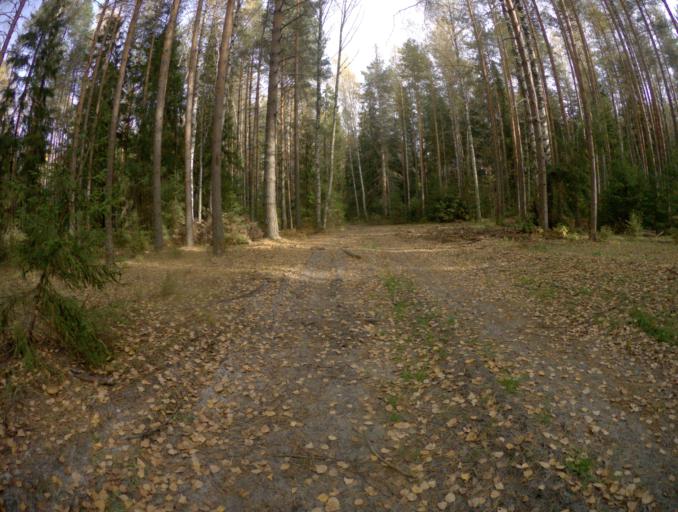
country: RU
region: Vladimir
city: Vorsha
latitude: 55.9378
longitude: 40.1297
